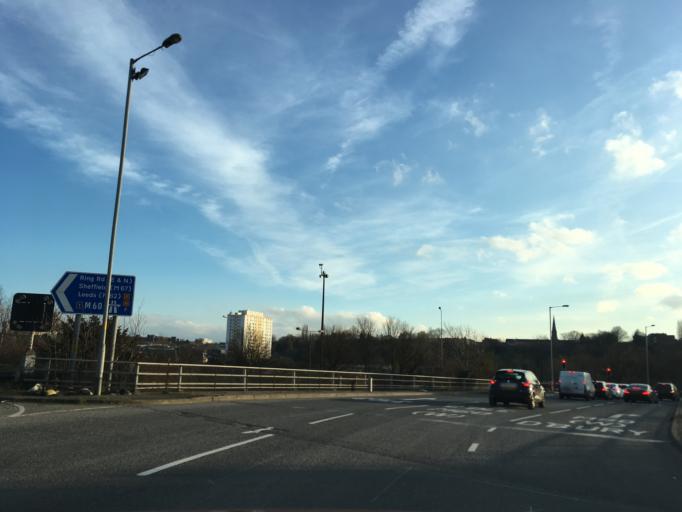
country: GB
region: England
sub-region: Borough of Stockport
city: Stockport
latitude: 53.4096
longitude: -2.1737
